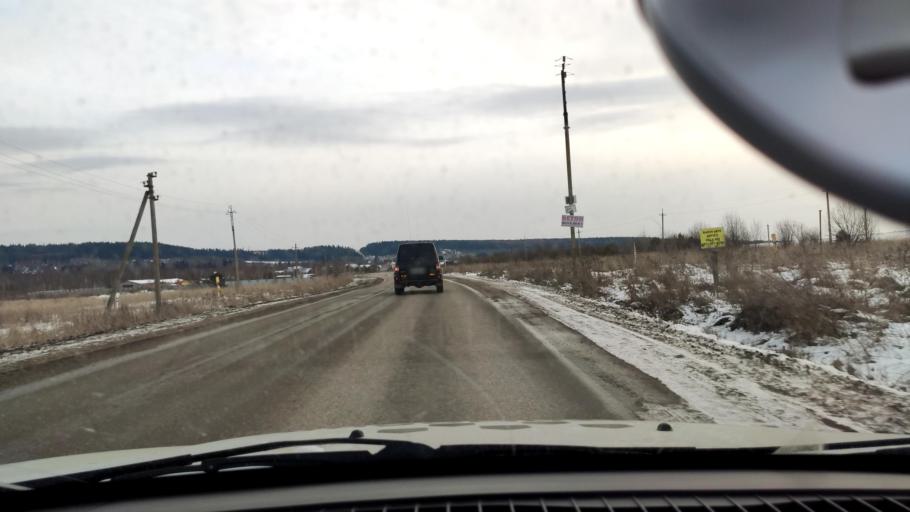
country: RU
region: Perm
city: Lobanovo
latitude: 57.8474
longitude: 56.3524
